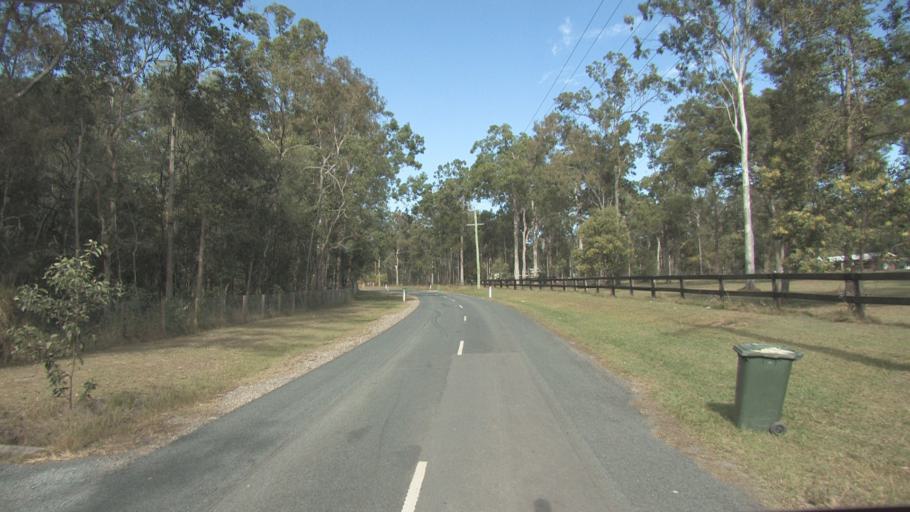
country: AU
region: Queensland
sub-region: Logan
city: North Maclean
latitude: -27.7513
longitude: 152.9734
